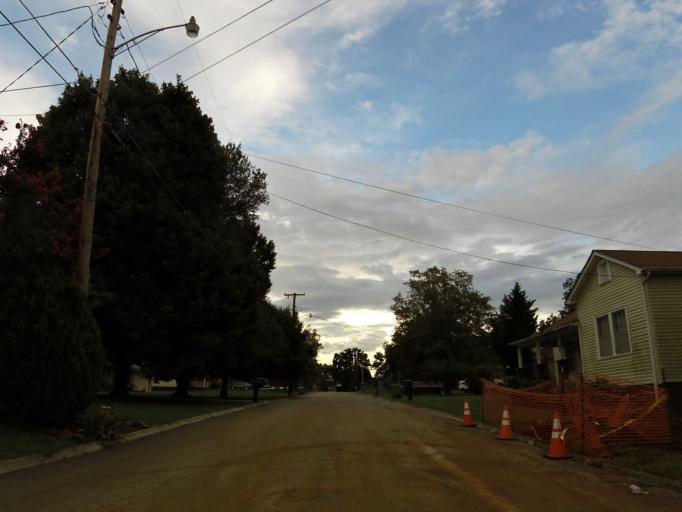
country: US
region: Tennessee
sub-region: Blount County
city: Maryville
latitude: 35.7612
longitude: -83.9530
